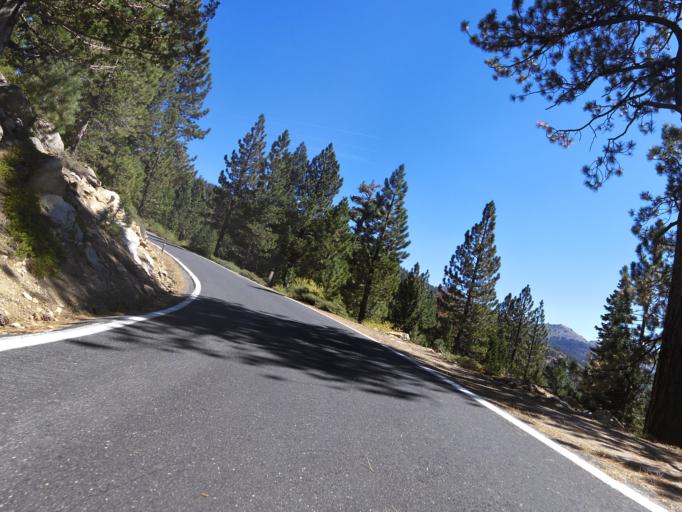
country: US
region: Nevada
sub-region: Douglas County
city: Gardnerville Ranchos
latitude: 38.5490
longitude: -119.8545
